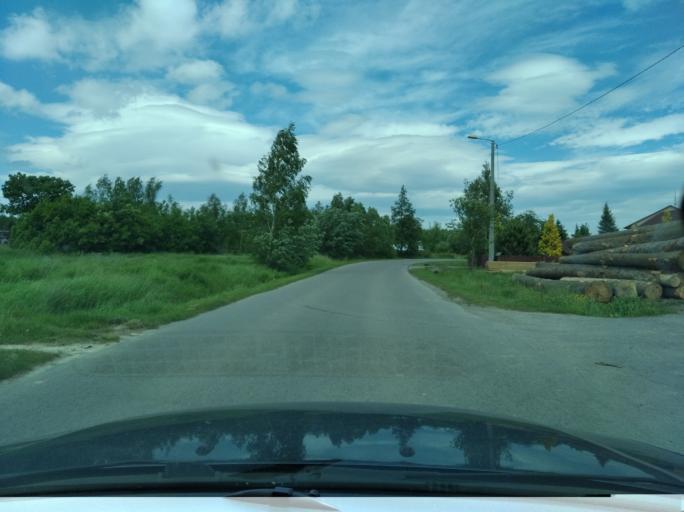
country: PL
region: Subcarpathian Voivodeship
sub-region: Powiat ropczycko-sedziszowski
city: Ropczyce
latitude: 50.0011
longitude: 21.6129
